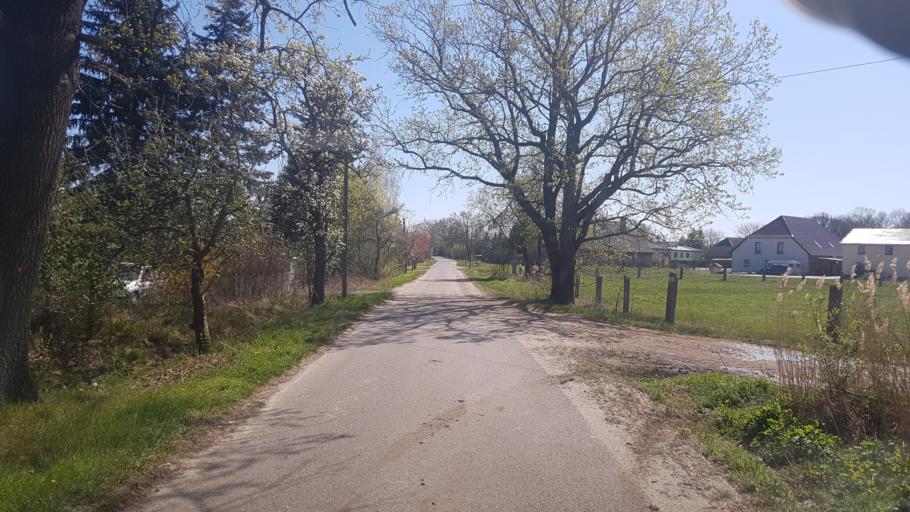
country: DE
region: Brandenburg
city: Sonnewalde
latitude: 51.7140
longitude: 13.6247
